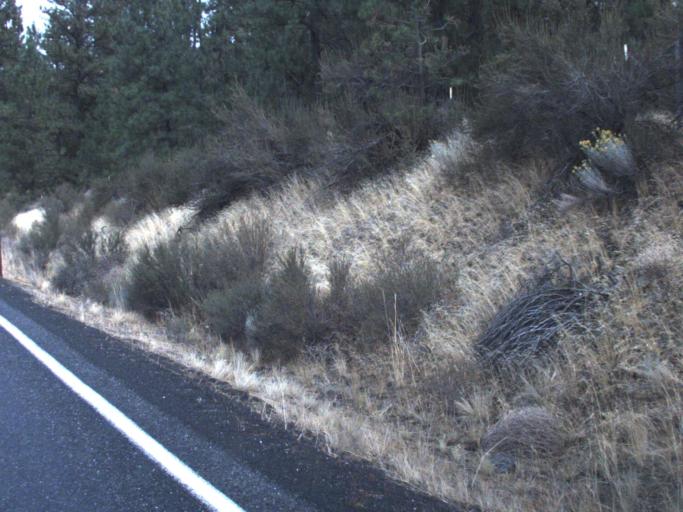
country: US
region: Washington
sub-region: Lincoln County
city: Davenport
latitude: 47.8073
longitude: -117.8931
